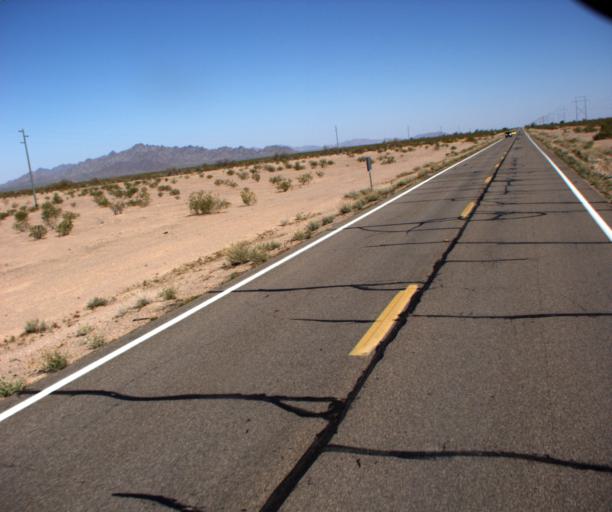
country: US
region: Arizona
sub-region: La Paz County
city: Quartzsite
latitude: 33.4268
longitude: -114.2170
